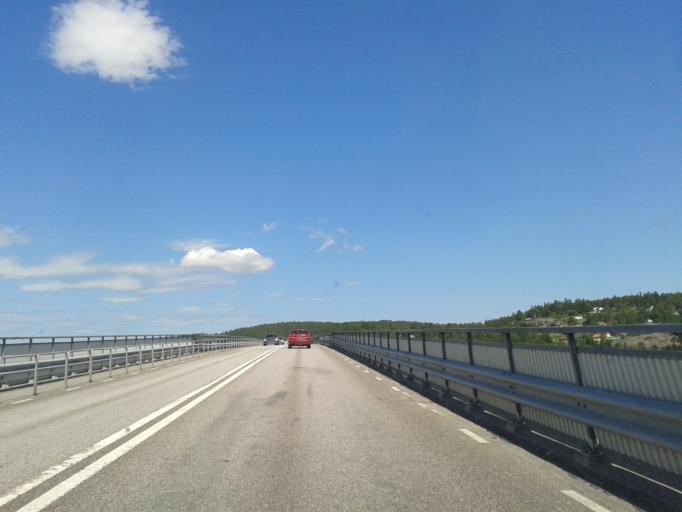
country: SE
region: Vaestra Goetaland
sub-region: Orust
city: Henan
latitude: 58.3042
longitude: 11.6996
